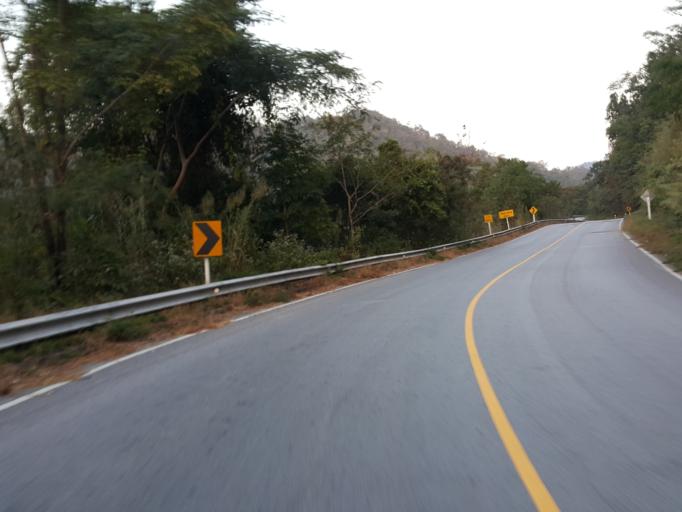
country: TH
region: Lampang
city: Thoen
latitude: 17.6841
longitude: 99.0776
